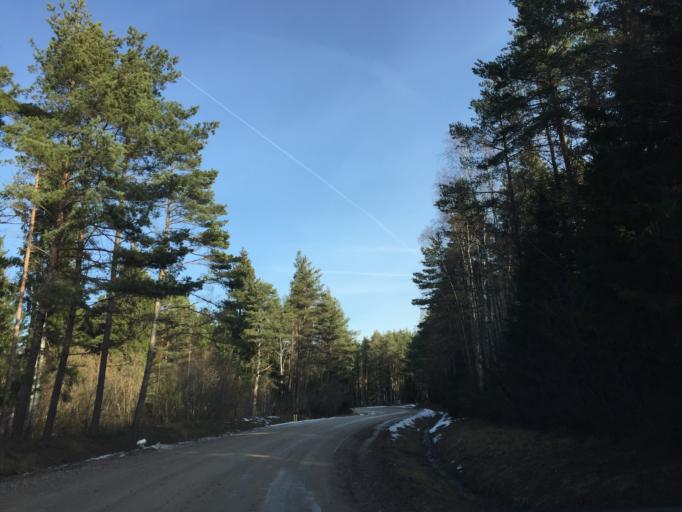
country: EE
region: Saare
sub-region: Kuressaare linn
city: Kuressaare
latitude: 58.3724
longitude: 22.0150
